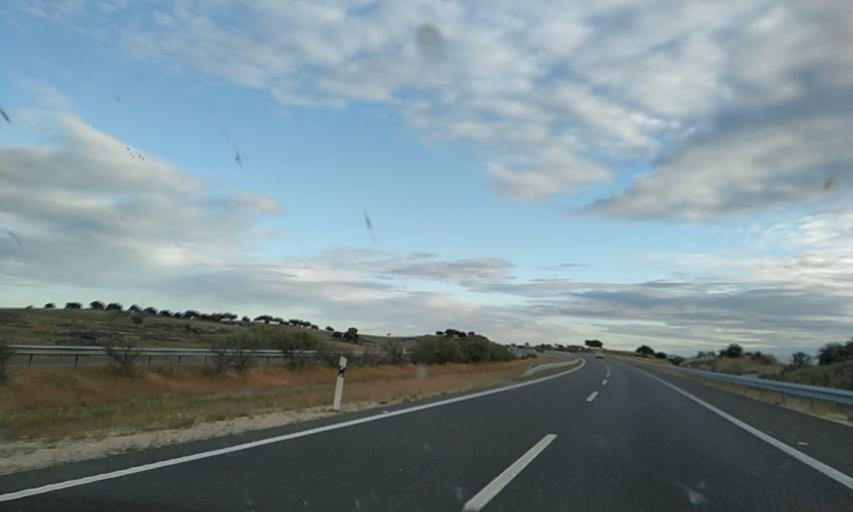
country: ES
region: Extremadura
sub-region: Provincia de Caceres
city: Casar de Caceres
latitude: 39.5018
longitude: -6.4380
